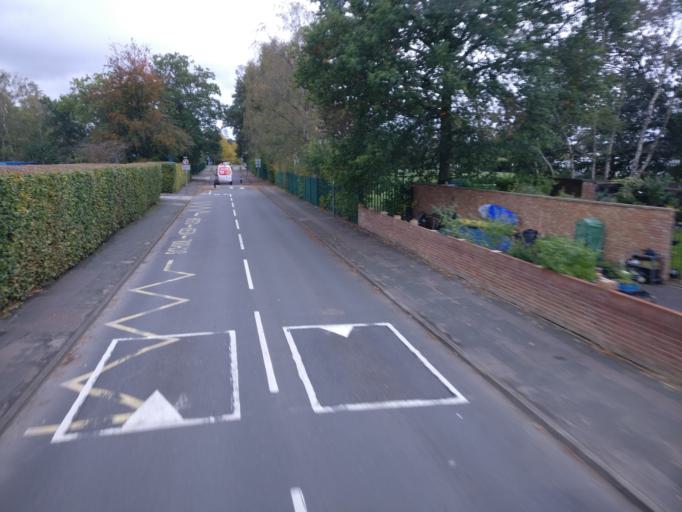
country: GB
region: England
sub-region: Surrey
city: Camberley
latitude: 51.3501
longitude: -0.7223
